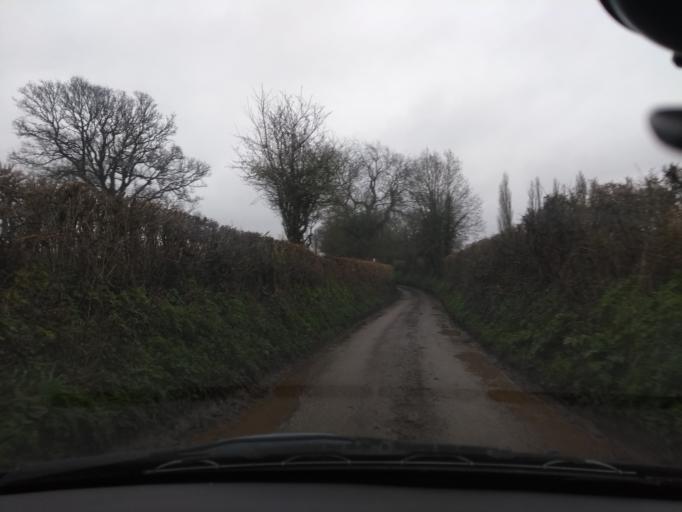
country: GB
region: England
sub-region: Somerset
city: Taunton
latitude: 51.0386
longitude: -3.1268
